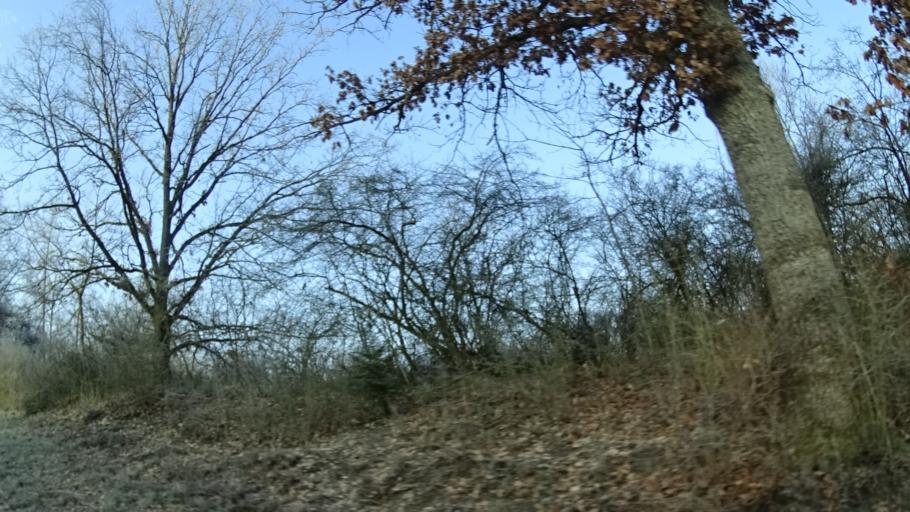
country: DE
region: Bavaria
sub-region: Upper Franconia
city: Weitramsdorf
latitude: 50.2390
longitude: 10.8796
